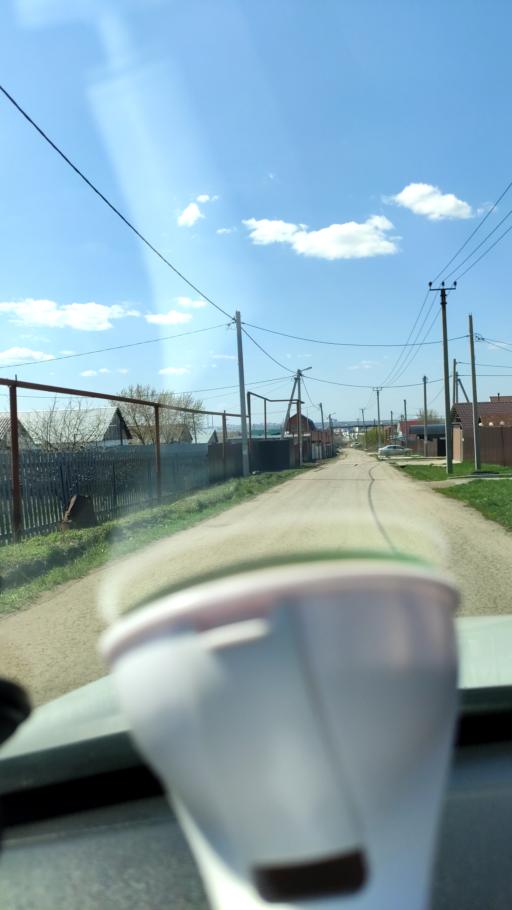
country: RU
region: Samara
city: Smyshlyayevka
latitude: 53.2647
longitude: 50.4167
